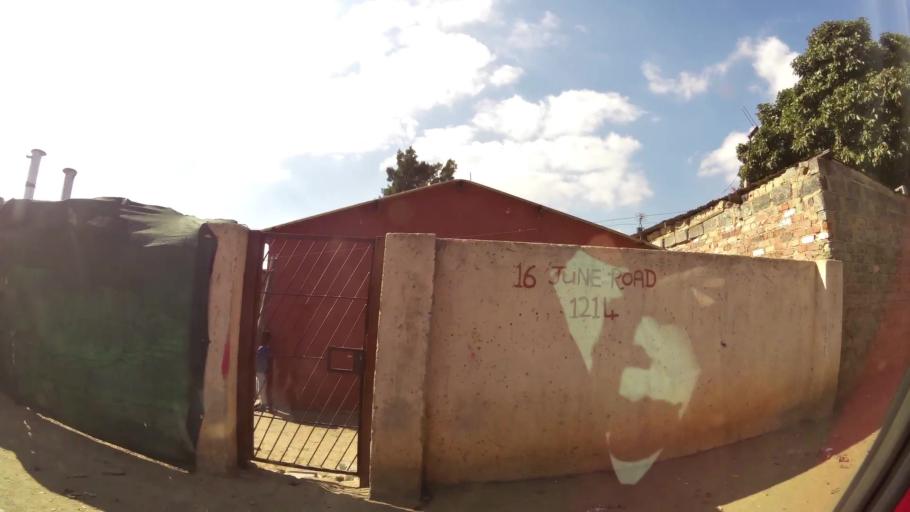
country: ZA
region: Gauteng
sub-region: Ekurhuleni Metropolitan Municipality
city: Tembisa
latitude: -26.0097
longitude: 28.1771
